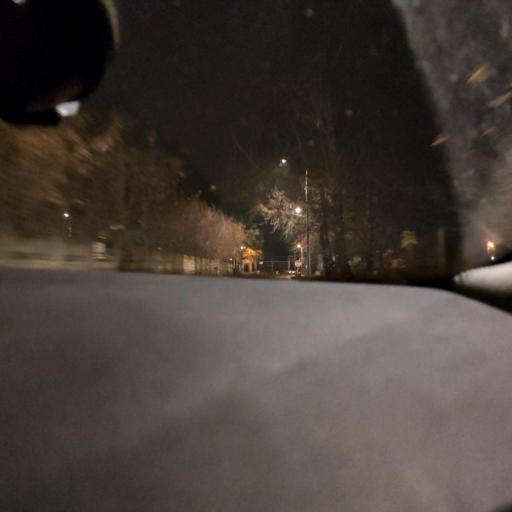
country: RU
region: Moskovskaya
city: Shcherbinka
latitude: 55.5164
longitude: 37.5223
